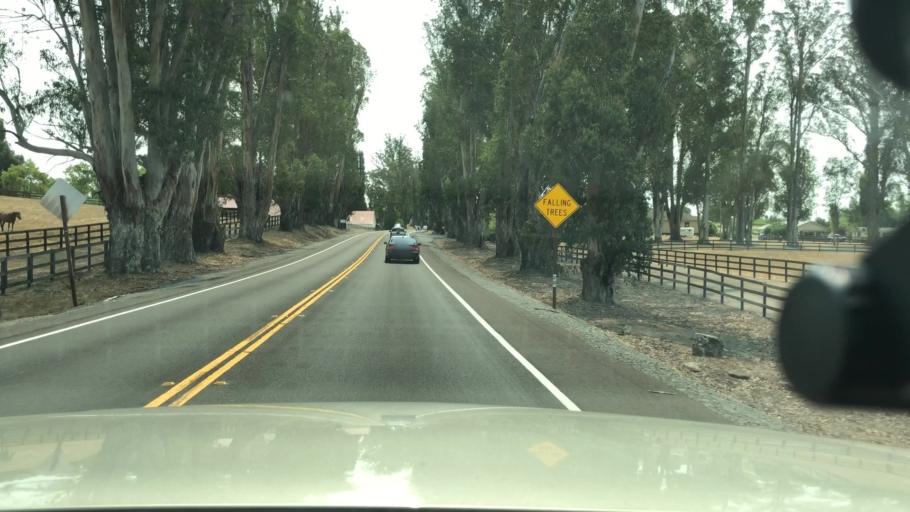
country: US
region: California
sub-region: Marin County
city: Black Point-Green Point
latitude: 38.1797
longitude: -122.5314
